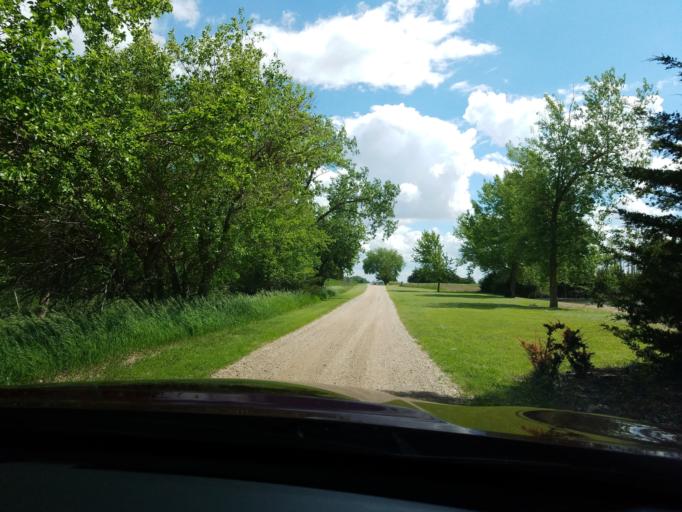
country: US
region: Nebraska
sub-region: Buffalo County
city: Kearney
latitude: 40.6558
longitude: -99.0086
